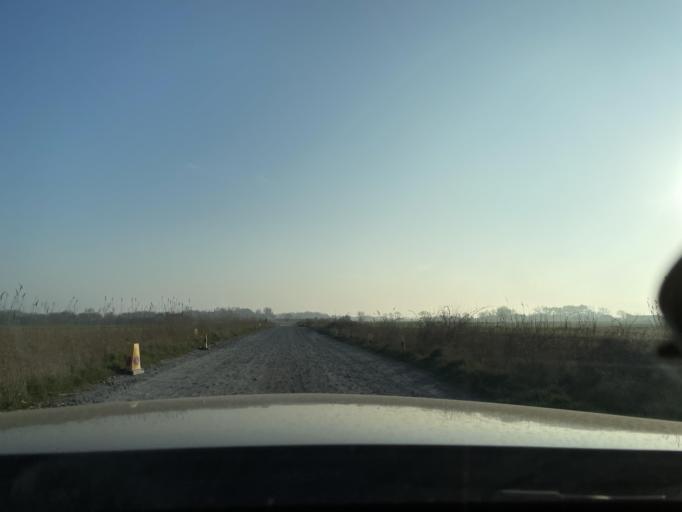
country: GB
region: England
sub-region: Norfolk
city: Martham
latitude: 52.7563
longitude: 1.6466
